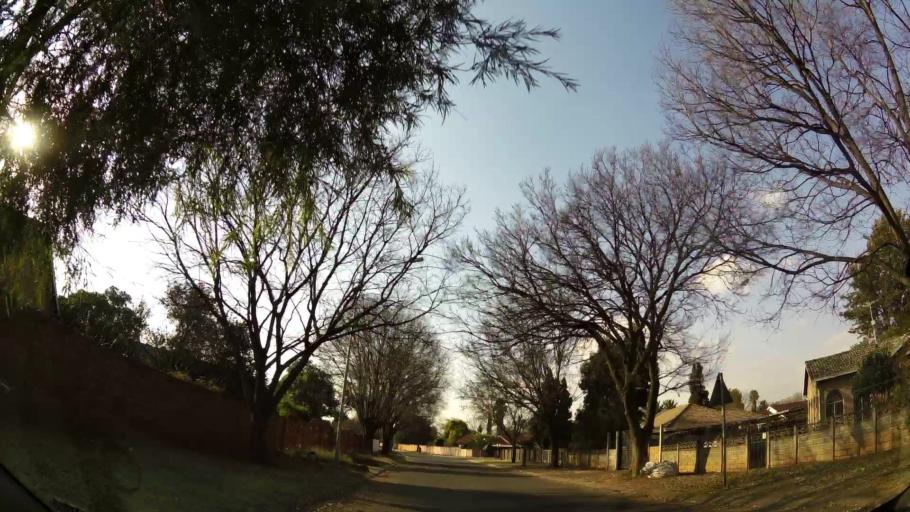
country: ZA
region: Gauteng
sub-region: Ekurhuleni Metropolitan Municipality
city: Benoni
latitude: -26.1288
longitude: 28.3708
